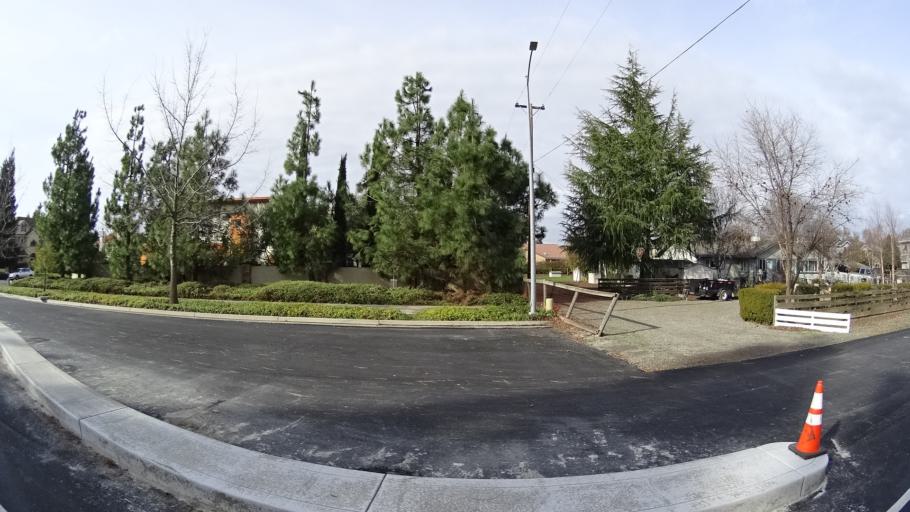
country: US
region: California
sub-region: Yolo County
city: Davis
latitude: 38.5417
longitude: -121.6946
